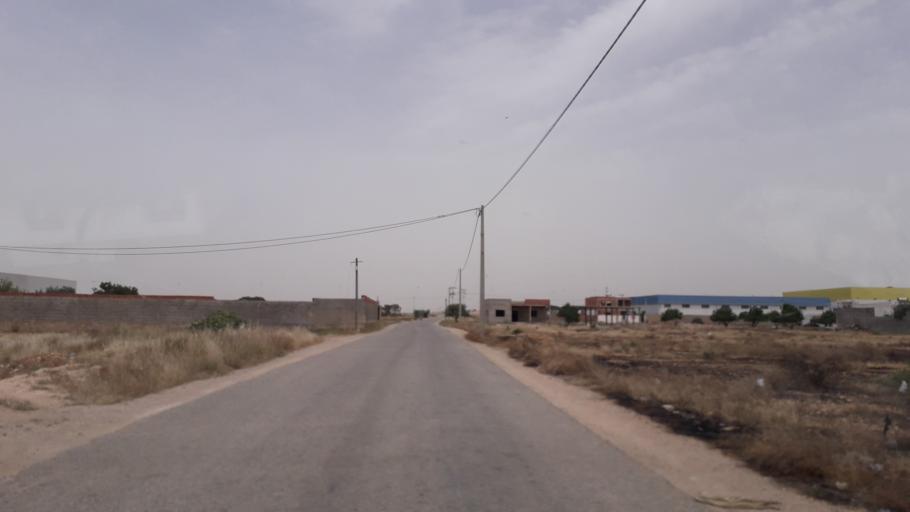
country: TN
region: Safaqis
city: Al Qarmadah
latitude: 34.8477
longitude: 10.7543
